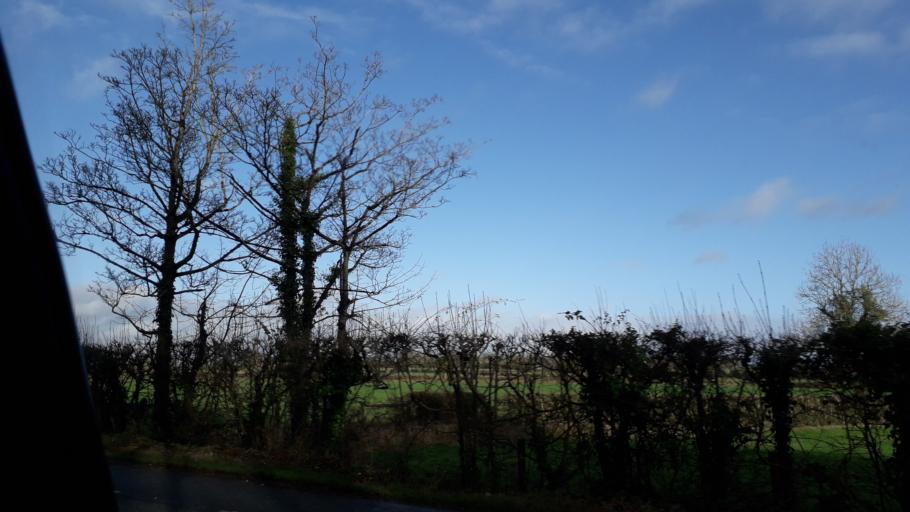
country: IE
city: Kentstown
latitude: 53.6320
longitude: -6.4928
